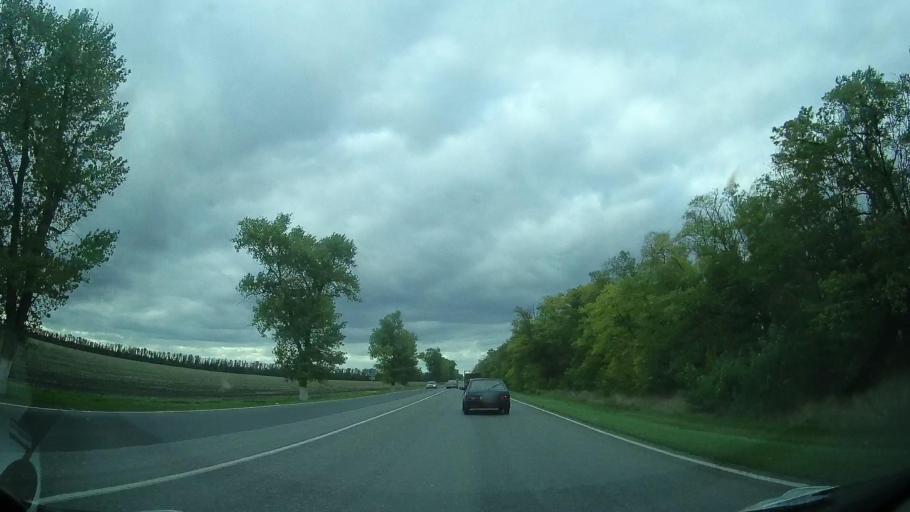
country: RU
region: Rostov
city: Zernograd
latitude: 46.8267
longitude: 40.2469
